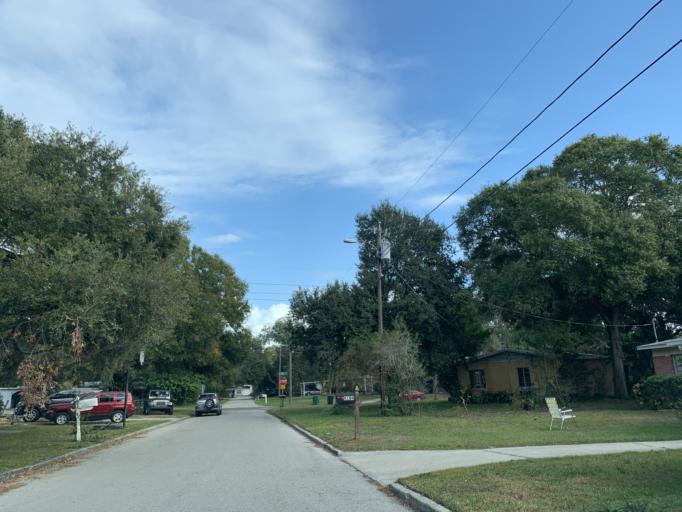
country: US
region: Florida
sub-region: Hillsborough County
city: Tampa
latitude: 27.9015
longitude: -82.5130
